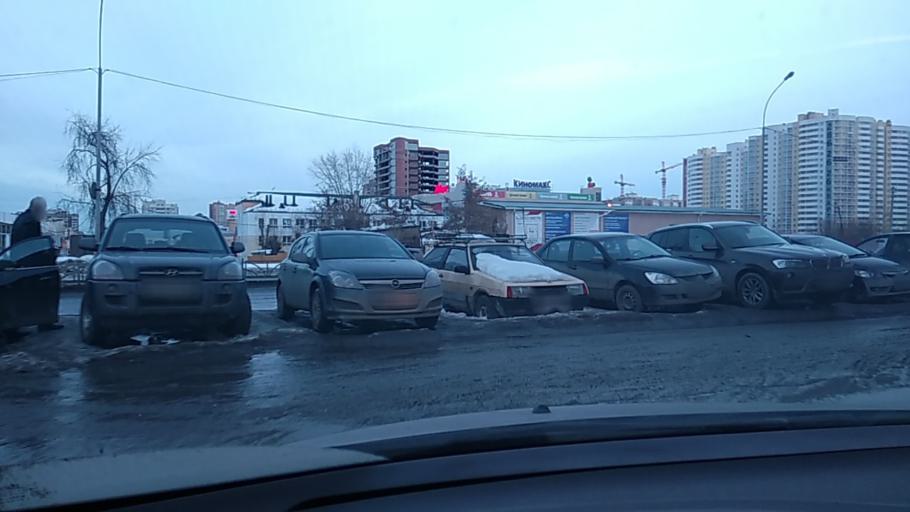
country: RU
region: Sverdlovsk
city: Yekaterinburg
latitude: 56.8079
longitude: 60.6069
